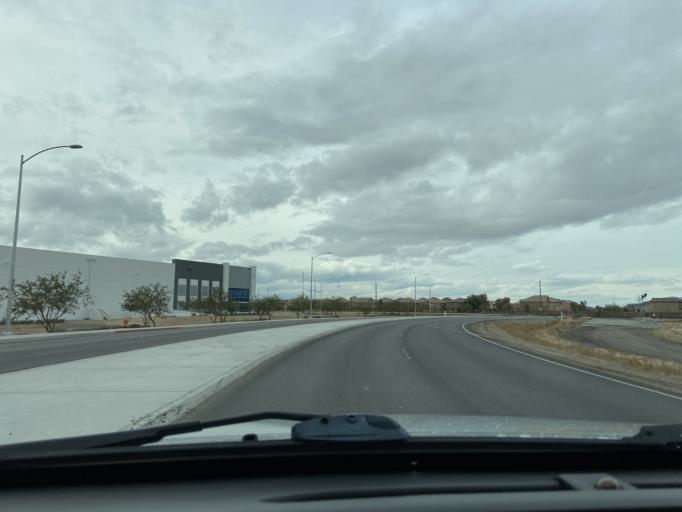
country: US
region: Nevada
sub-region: Clark County
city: Nellis Air Force Base
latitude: 36.2619
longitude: -115.0815
